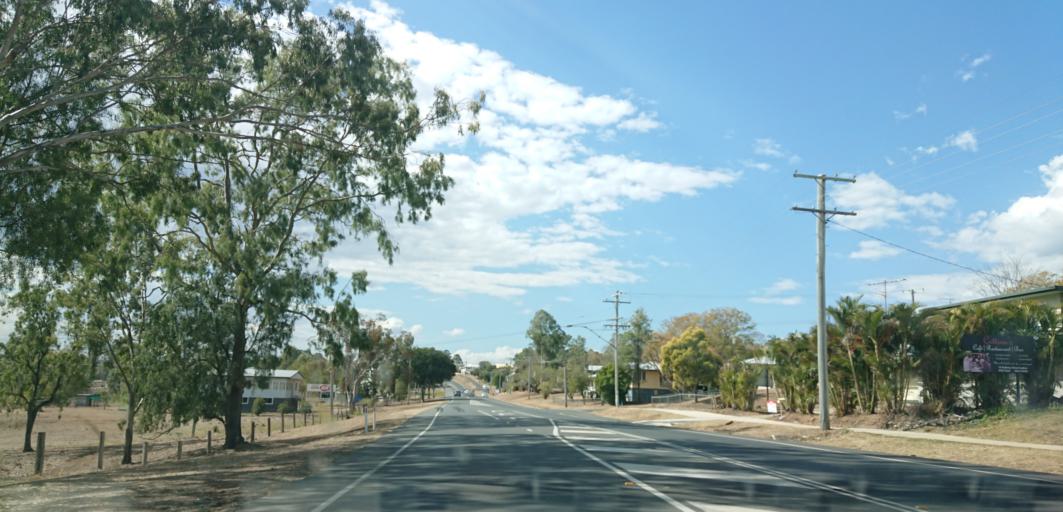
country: AU
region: Queensland
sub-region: Lockyer Valley
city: Gatton
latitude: -27.5679
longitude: 152.2711
